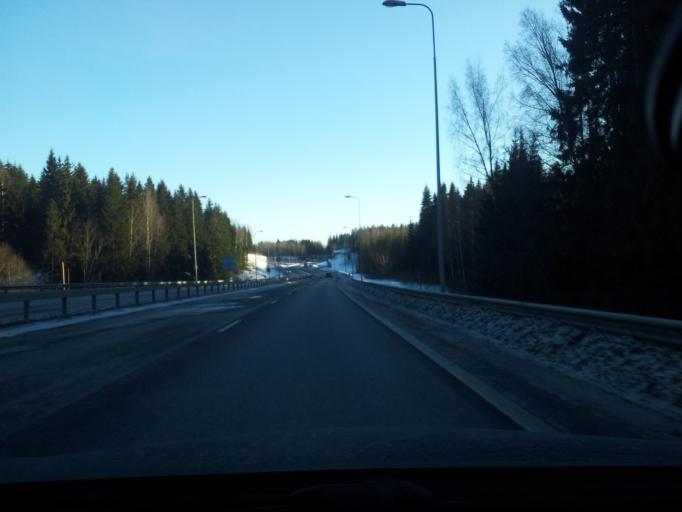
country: FI
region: Uusimaa
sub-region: Helsinki
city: Vihti
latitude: 60.2989
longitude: 24.3597
